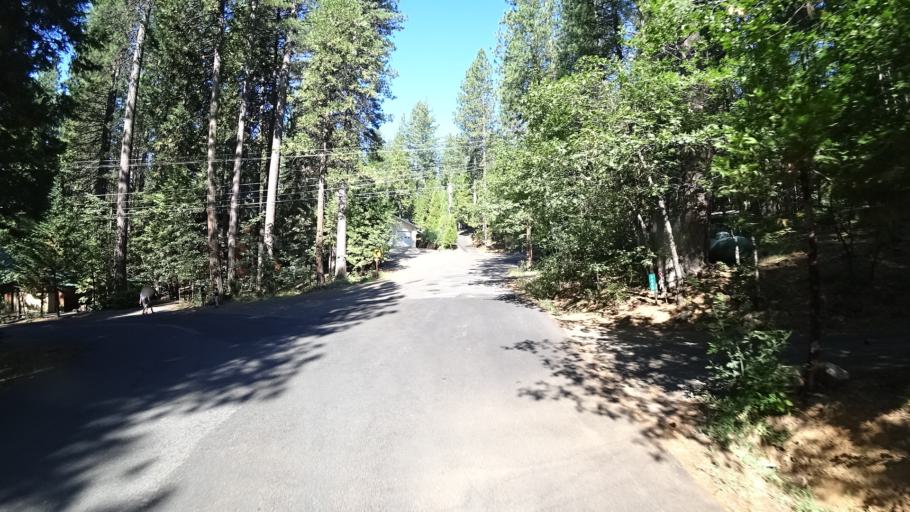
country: US
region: California
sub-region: Calaveras County
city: Arnold
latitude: 38.2537
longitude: -120.3590
